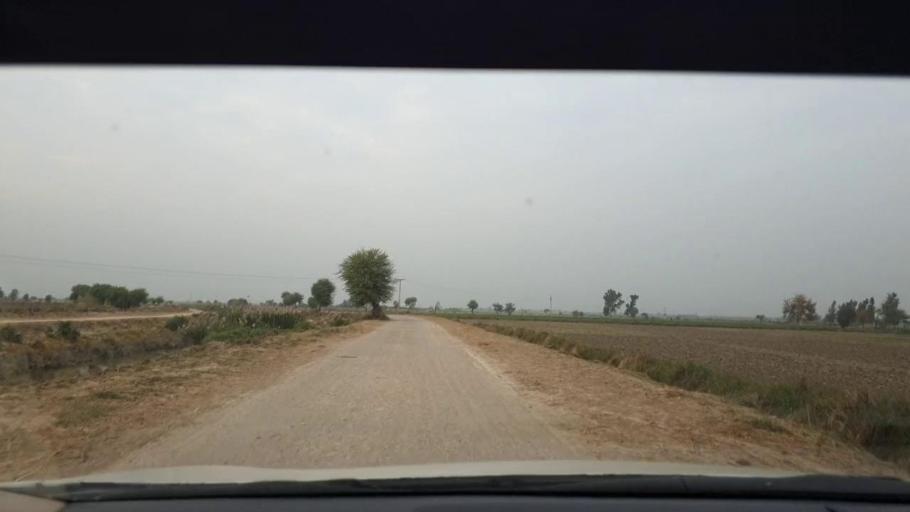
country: PK
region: Sindh
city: Sinjhoro
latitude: 25.9146
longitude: 68.7584
